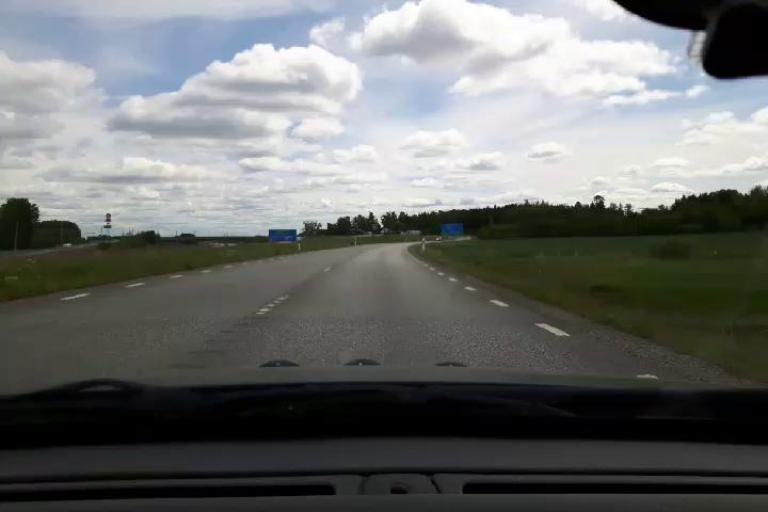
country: SE
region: Uppsala
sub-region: Tierps Kommun
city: Tierp
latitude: 60.3432
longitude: 17.4801
